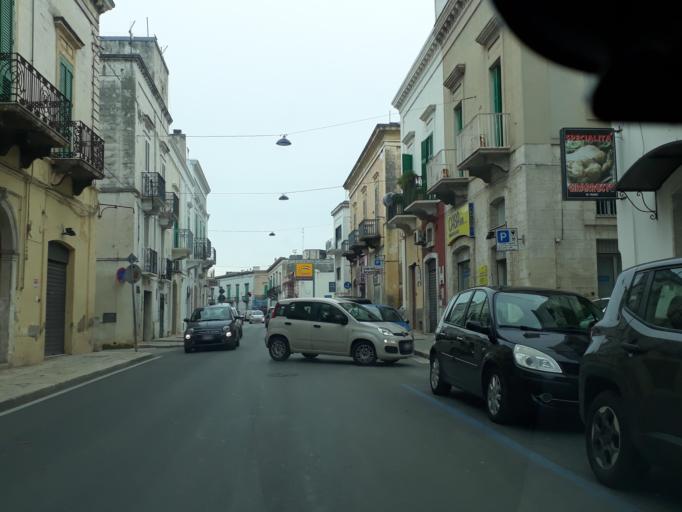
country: IT
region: Apulia
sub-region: Provincia di Brindisi
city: Fasano
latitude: 40.8368
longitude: 17.3610
